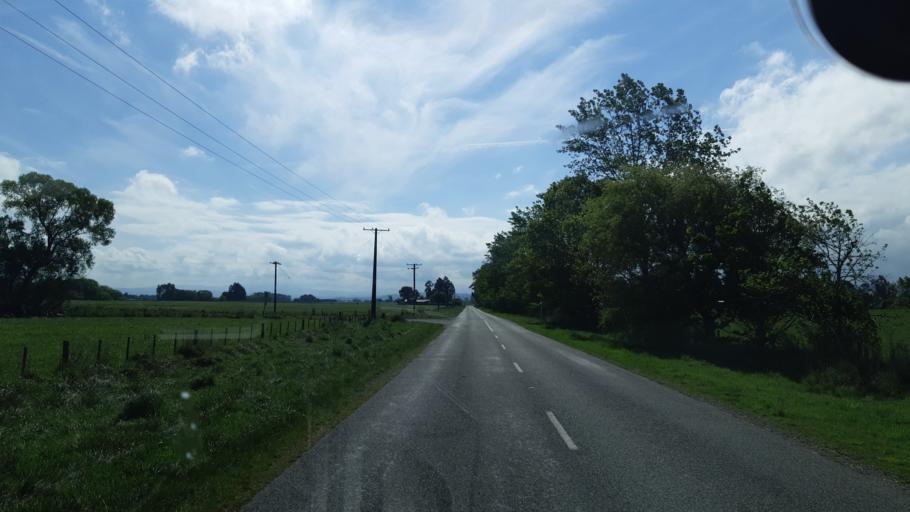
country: NZ
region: Canterbury
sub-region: Timaru District
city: Pleasant Point
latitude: -44.2262
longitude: 171.1941
